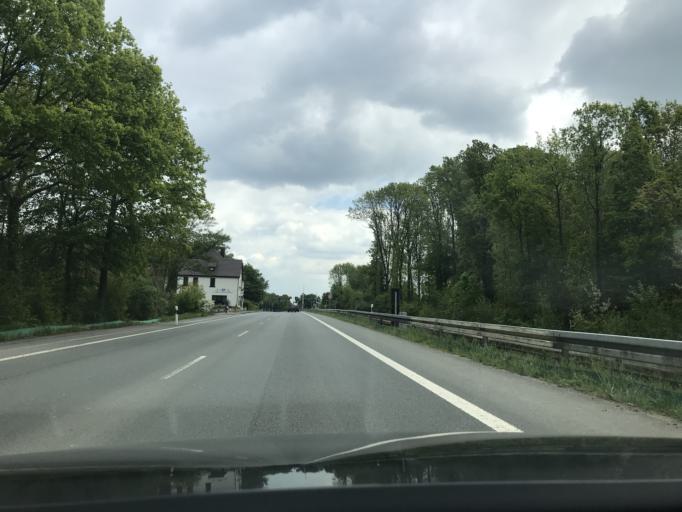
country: DE
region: North Rhine-Westphalia
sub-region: Regierungsbezirk Detmold
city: Rheda-Wiedenbruck
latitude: 51.8671
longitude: 8.2642
